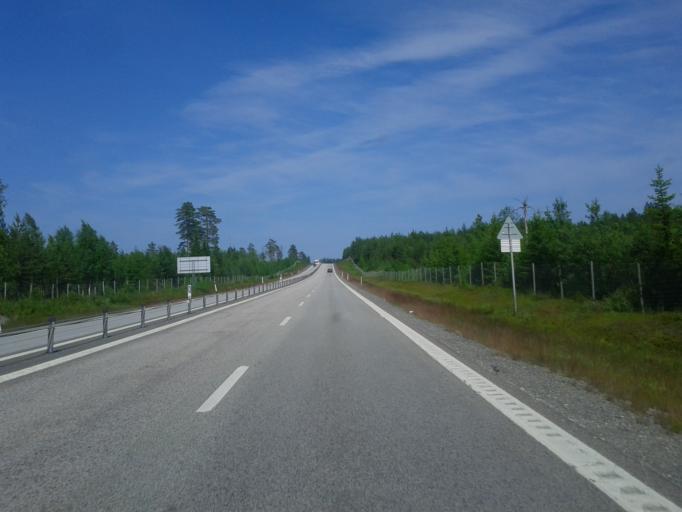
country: SE
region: Vaesterbotten
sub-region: Umea Kommun
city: Hoernefors
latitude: 63.6429
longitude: 19.9284
